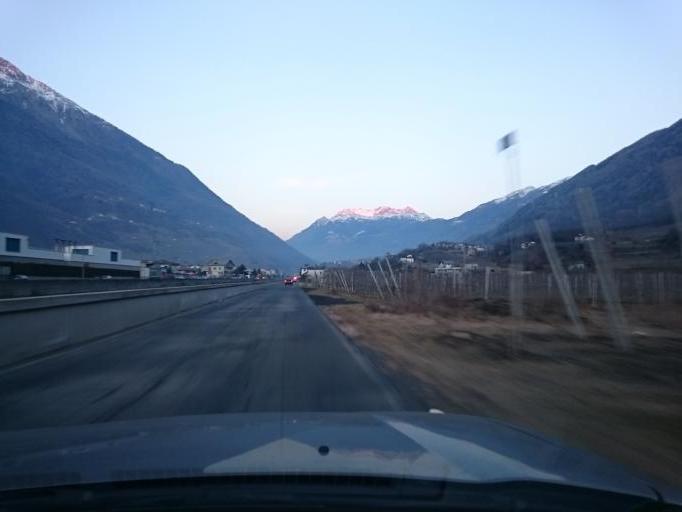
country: IT
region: Lombardy
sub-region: Provincia di Sondrio
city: Tirano
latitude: 46.2075
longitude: 10.1579
